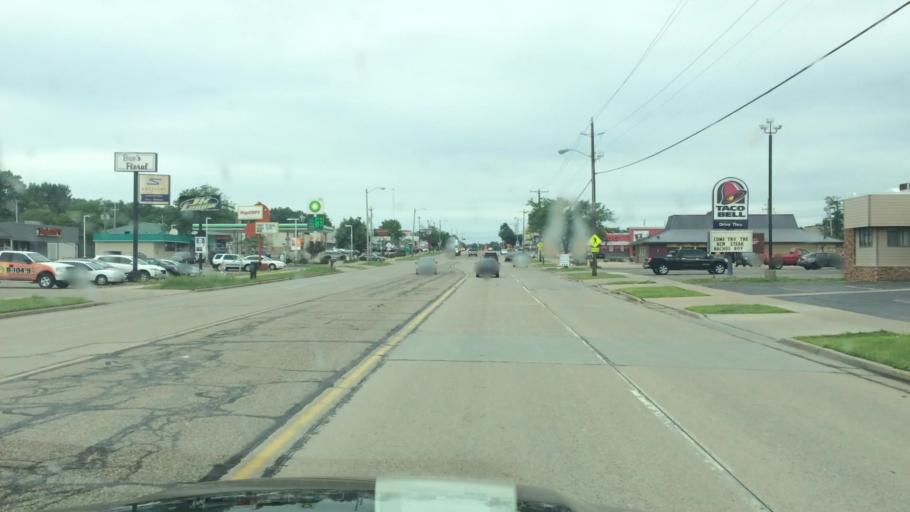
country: US
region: Wisconsin
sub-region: Portage County
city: Stevens Point
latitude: 44.5301
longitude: -89.5748
